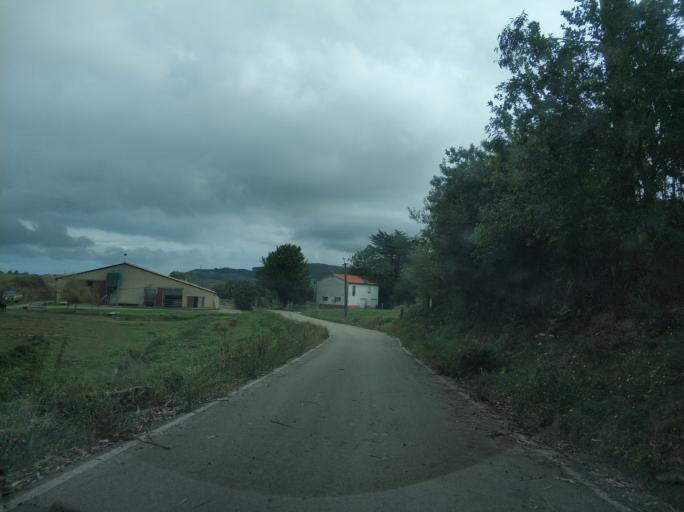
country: ES
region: Cantabria
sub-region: Provincia de Cantabria
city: San Miguel de Meruelo
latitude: 43.4347
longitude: -3.5747
